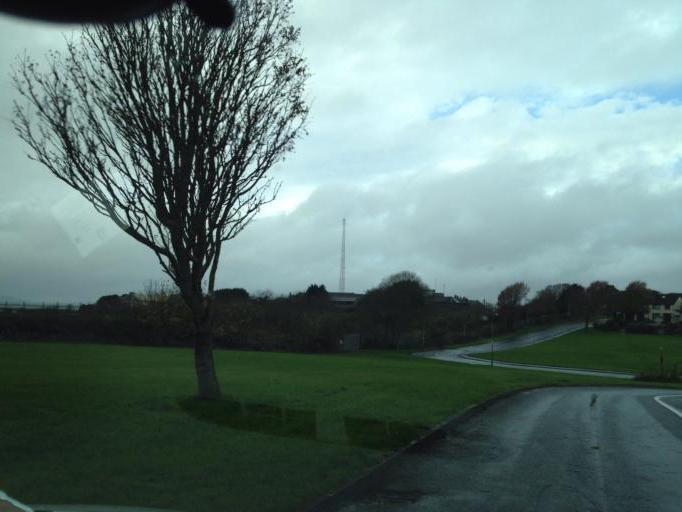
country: IE
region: Connaught
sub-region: County Galway
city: Gaillimh
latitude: 53.2725
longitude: -9.0237
